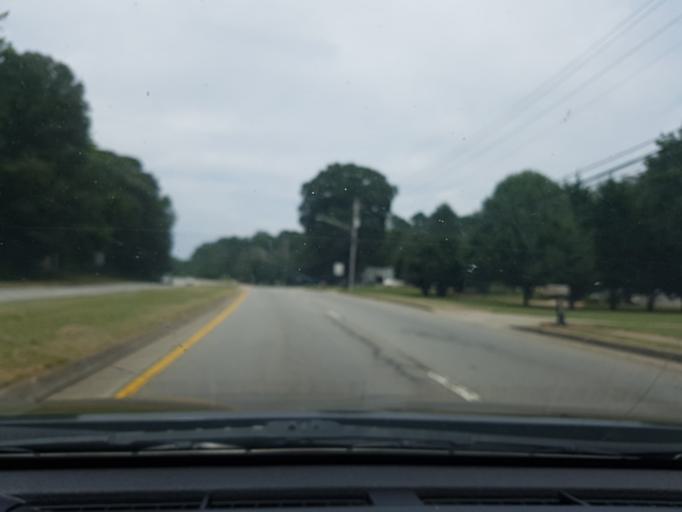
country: US
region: Georgia
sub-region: Gwinnett County
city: Suwanee
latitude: 34.0143
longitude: -84.0414
